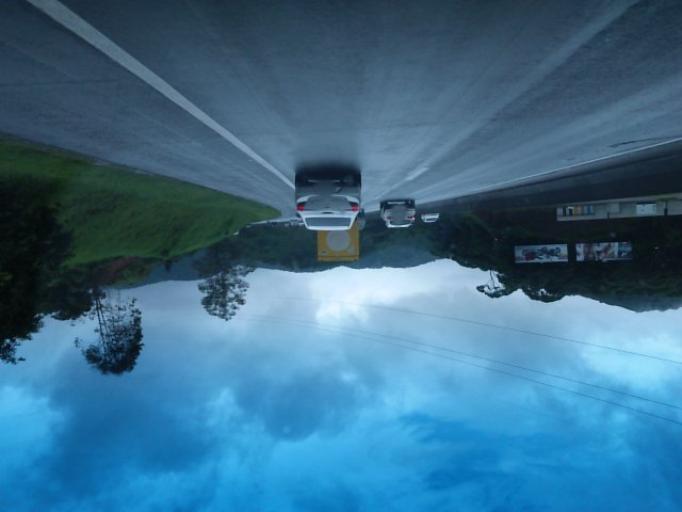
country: BR
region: Santa Catarina
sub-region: Balneario Camboriu
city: Balneario Camboriu
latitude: -26.9651
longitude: -48.6835
